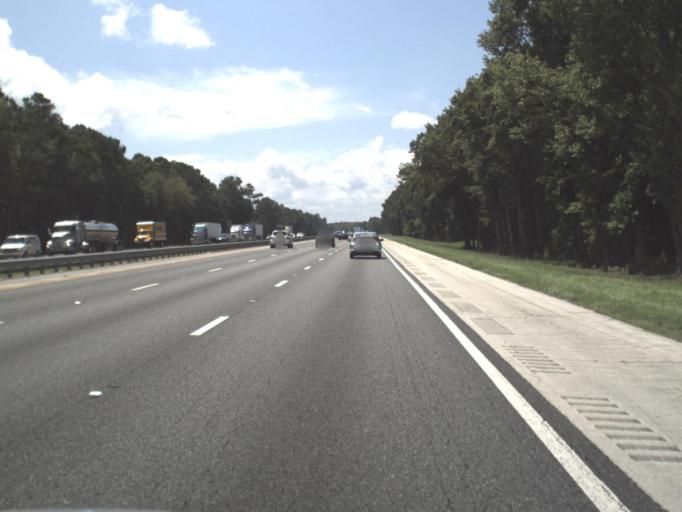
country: US
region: Florida
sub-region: Saint Johns County
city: Villano Beach
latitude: 29.9666
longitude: -81.4502
